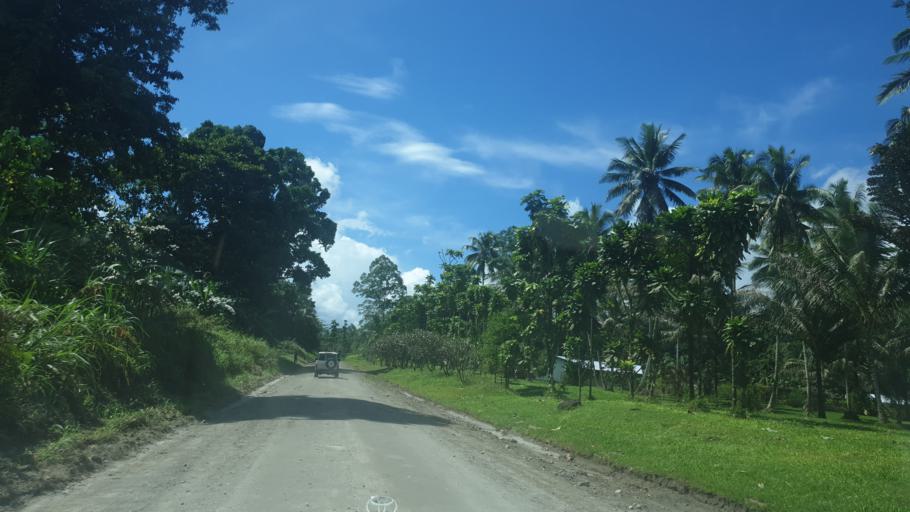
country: PG
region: Bougainville
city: Panguna
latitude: -6.6602
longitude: 155.4431
